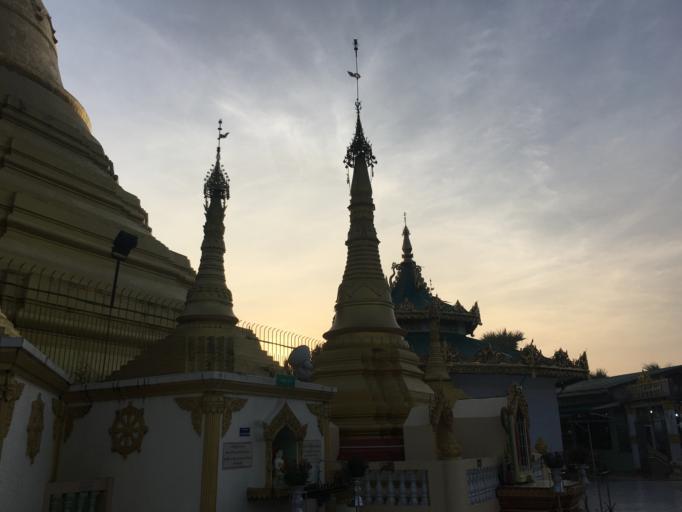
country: MM
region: Mon
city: Mawlamyine
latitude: 16.4731
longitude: 97.6295
